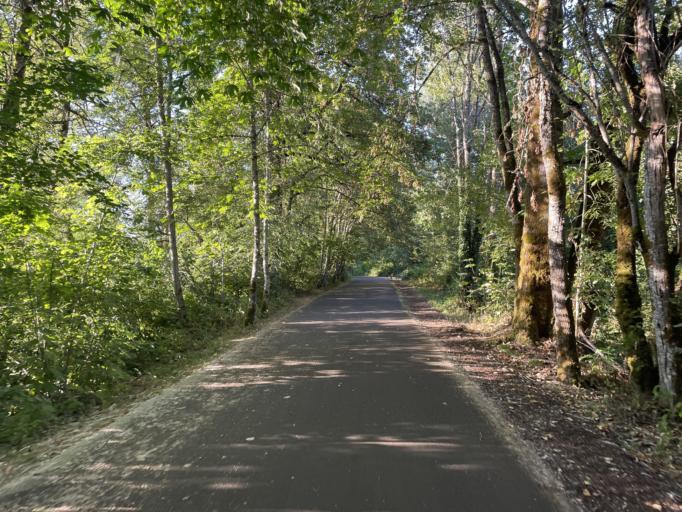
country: US
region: Oregon
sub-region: Marion County
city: Salem
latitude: 44.9200
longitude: -123.0753
